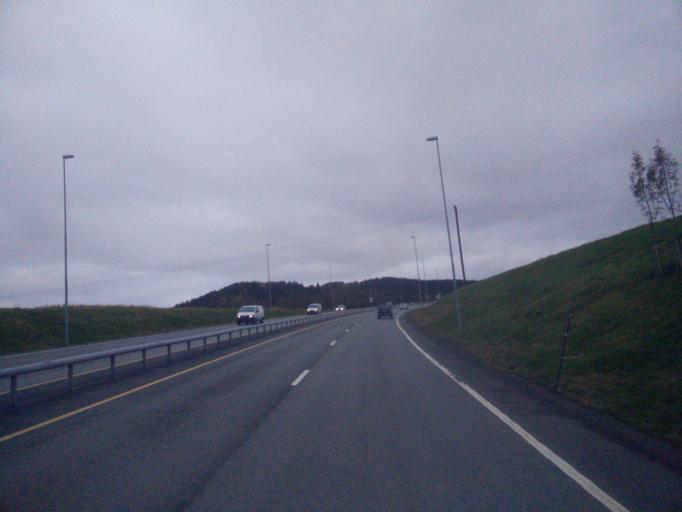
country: NO
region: Nord-Trondelag
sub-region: Stjordal
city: Stjordal
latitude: 63.4853
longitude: 10.8891
